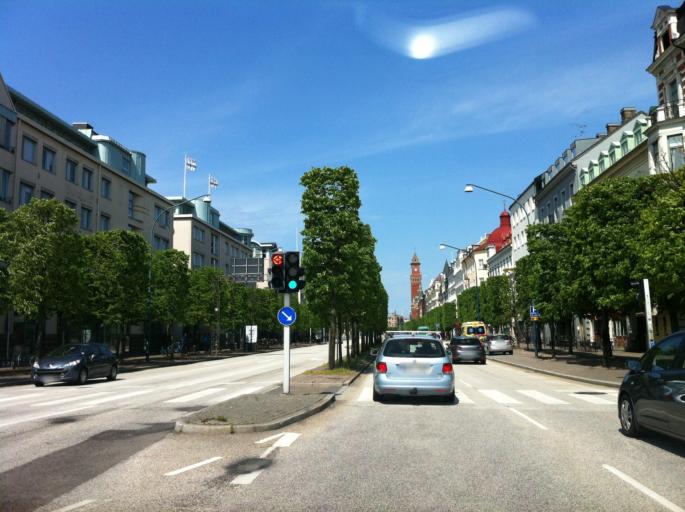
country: SE
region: Skane
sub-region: Helsingborg
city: Glumslov
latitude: 55.9582
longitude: 12.8332
